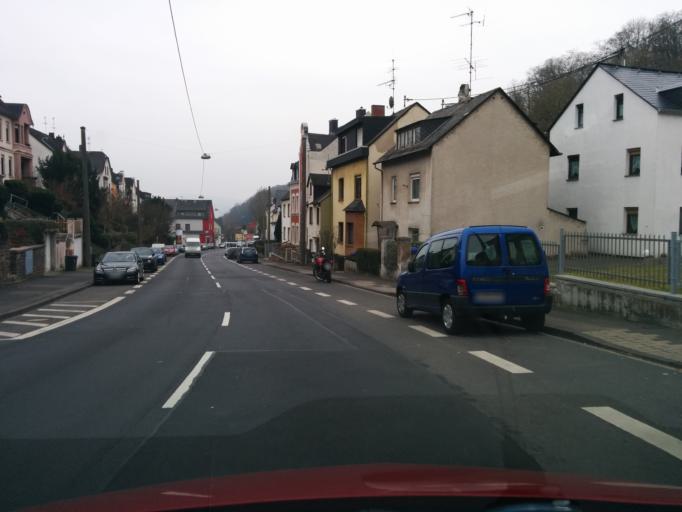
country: DE
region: Rheinland-Pfalz
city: Urbar
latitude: 50.3711
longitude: 7.6253
